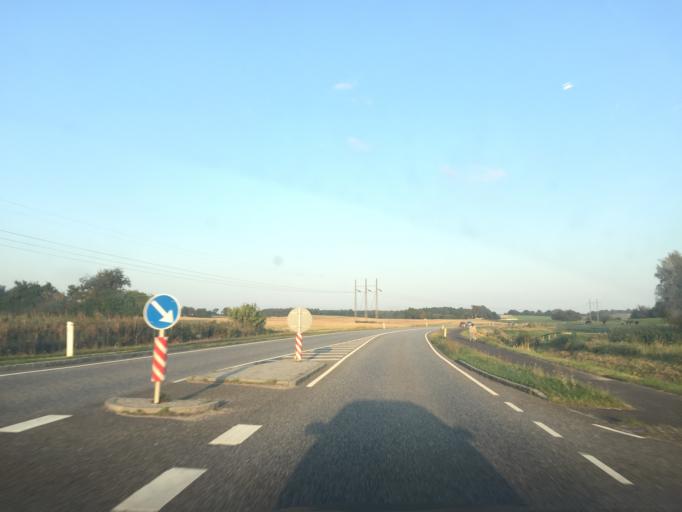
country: DK
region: Zealand
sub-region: Lejre Kommune
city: Kirke Hvalso
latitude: 55.5841
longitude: 11.9007
